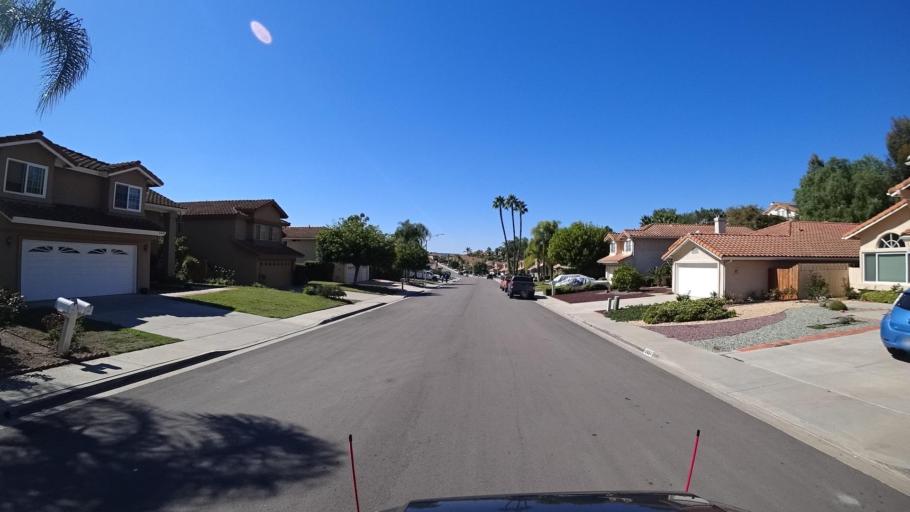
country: US
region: California
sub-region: San Diego County
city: Rancho San Diego
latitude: 32.7467
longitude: -116.9161
